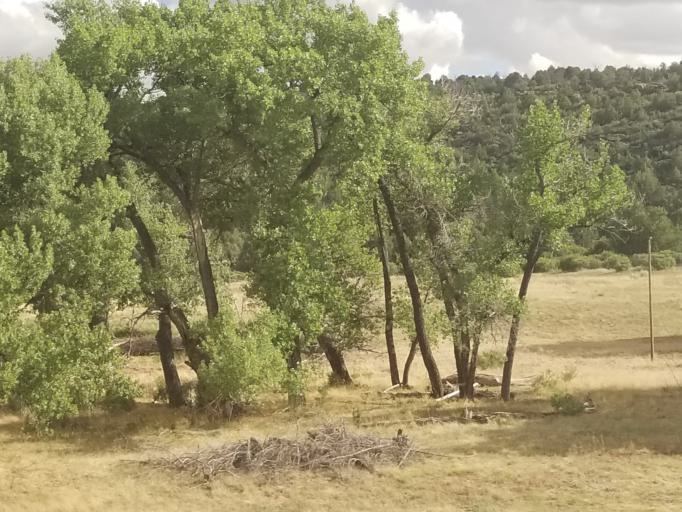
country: US
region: New Mexico
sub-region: San Miguel County
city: Las Vegas
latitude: 35.8168
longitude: -104.8831
